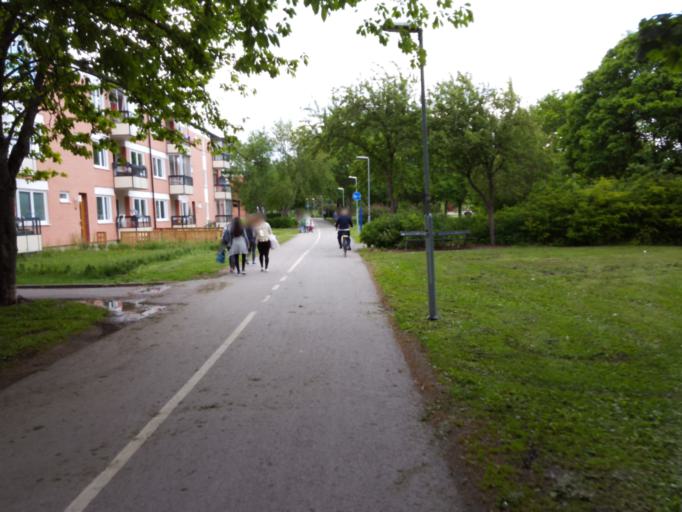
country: SE
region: Uppsala
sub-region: Uppsala Kommun
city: Uppsala
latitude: 59.8733
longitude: 17.6582
